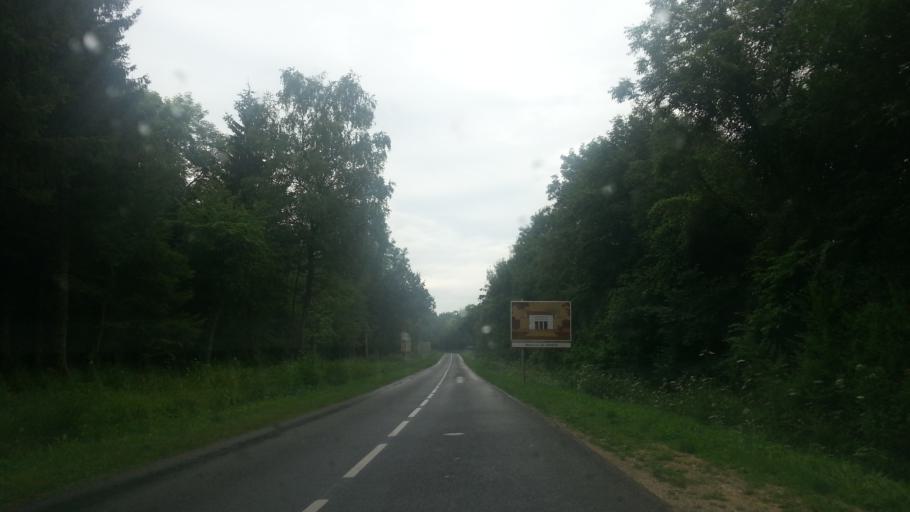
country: FR
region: Lorraine
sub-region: Departement de la Meuse
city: Verdun
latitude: 49.2013
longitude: 5.4241
